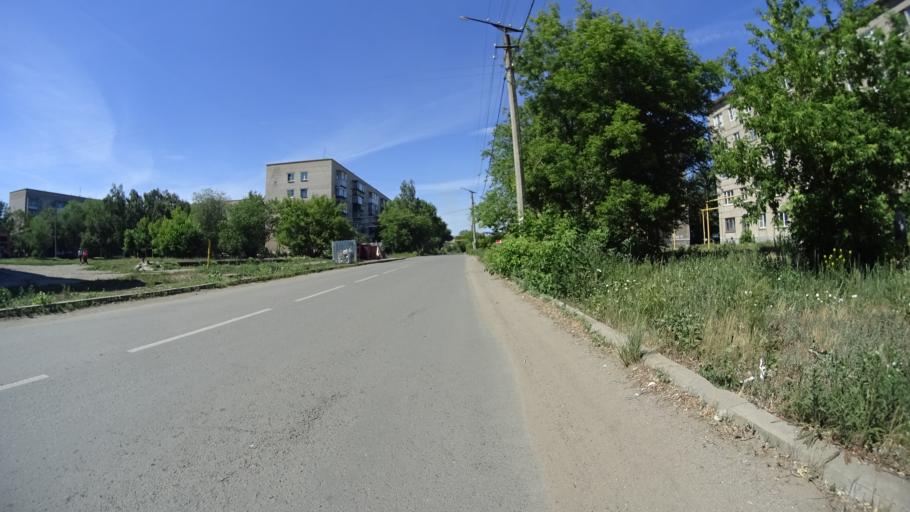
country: RU
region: Chelyabinsk
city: Troitsk
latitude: 54.0917
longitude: 61.5501
